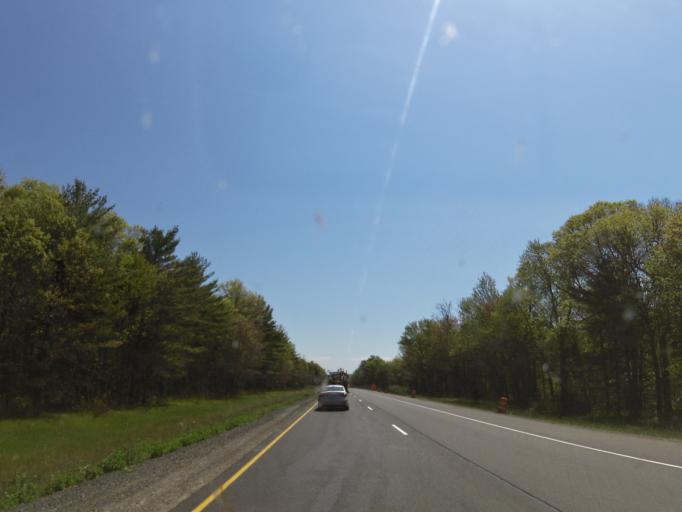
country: US
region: Wisconsin
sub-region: Jackson County
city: Black River Falls
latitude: 44.2440
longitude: -90.7356
